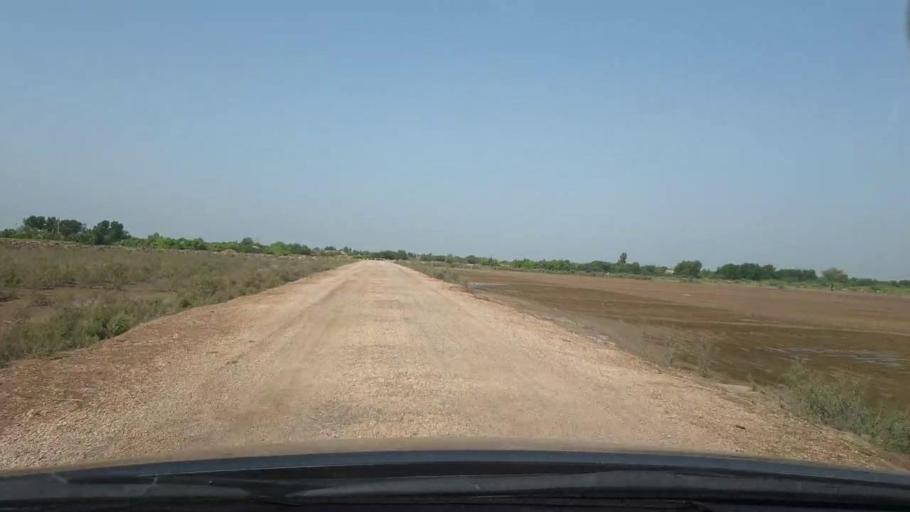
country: PK
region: Sindh
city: Tando Bago
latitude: 24.7179
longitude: 69.1059
